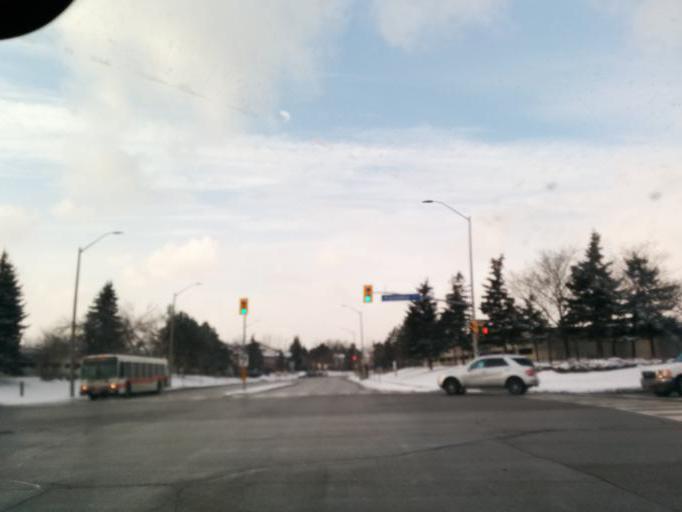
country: CA
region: Ontario
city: Brampton
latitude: 43.5863
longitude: -79.7586
